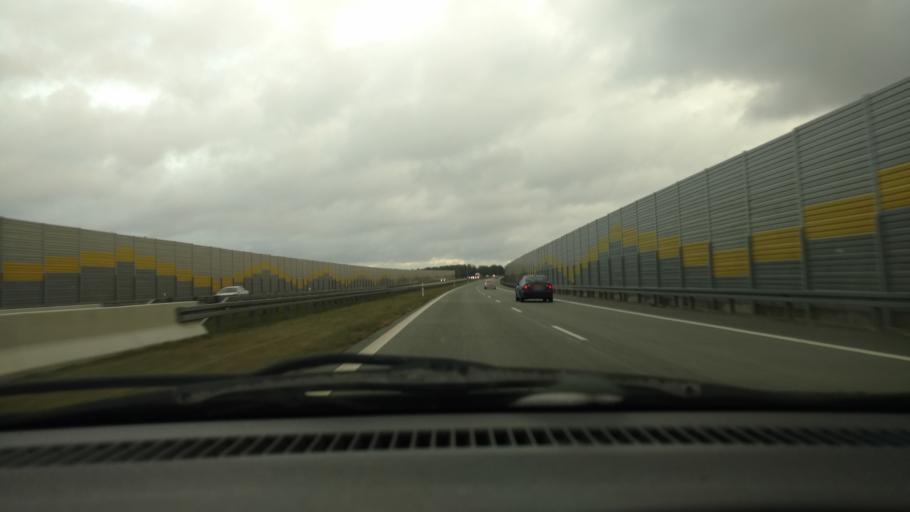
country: PL
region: Lodz Voivodeship
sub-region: Powiat pabianicki
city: Pabianice
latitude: 51.6217
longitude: 19.3839
